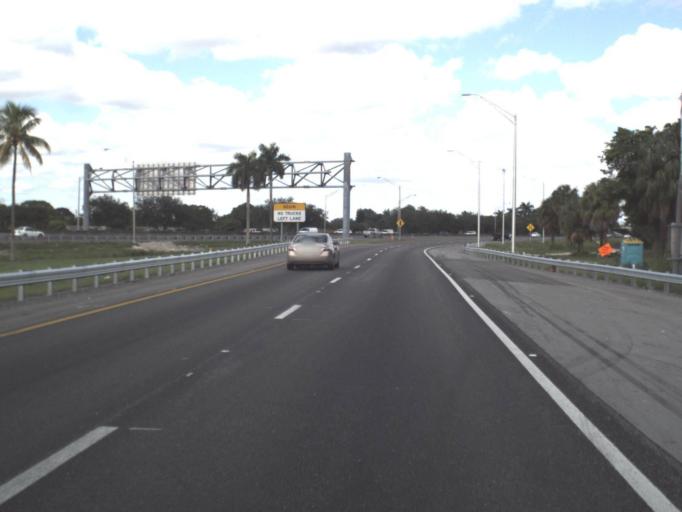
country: US
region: Florida
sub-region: Broward County
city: Miramar
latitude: 25.9768
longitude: -80.2289
